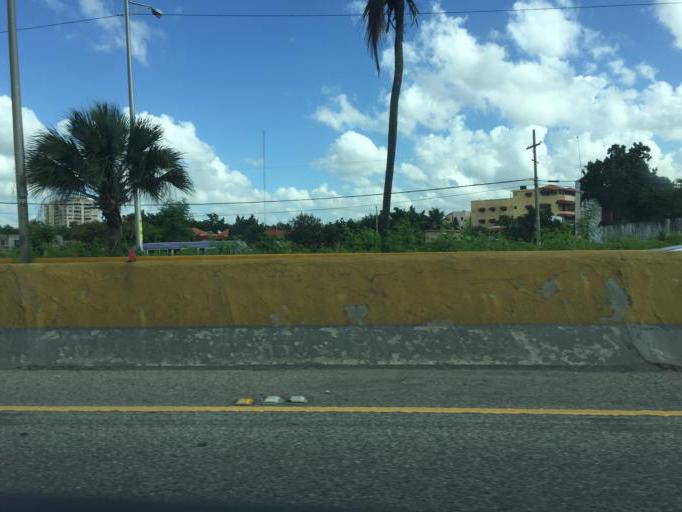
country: DO
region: Santo Domingo
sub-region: Santo Domingo
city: Santo Domingo Este
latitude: 18.4797
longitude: -69.8378
